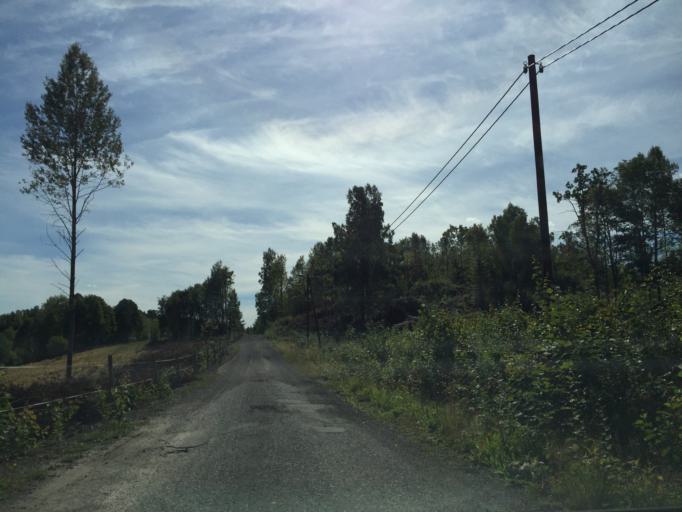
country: NO
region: Vestfold
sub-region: Hof
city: Hof
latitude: 59.4564
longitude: 10.1475
